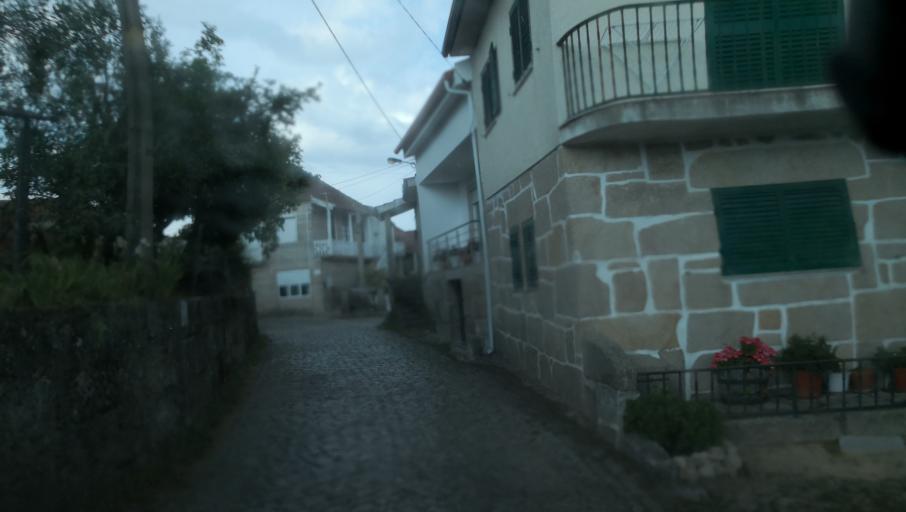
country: PT
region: Vila Real
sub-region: Vila Real
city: Vila Real
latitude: 41.3566
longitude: -7.6988
